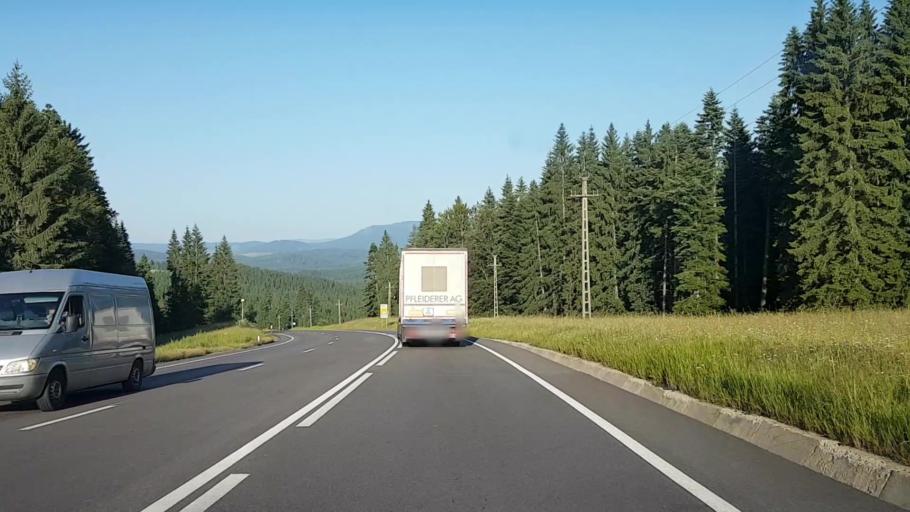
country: RO
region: Suceava
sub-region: Comuna Poiana Stampei
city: Poiana Stampei
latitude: 47.2841
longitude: 25.0475
